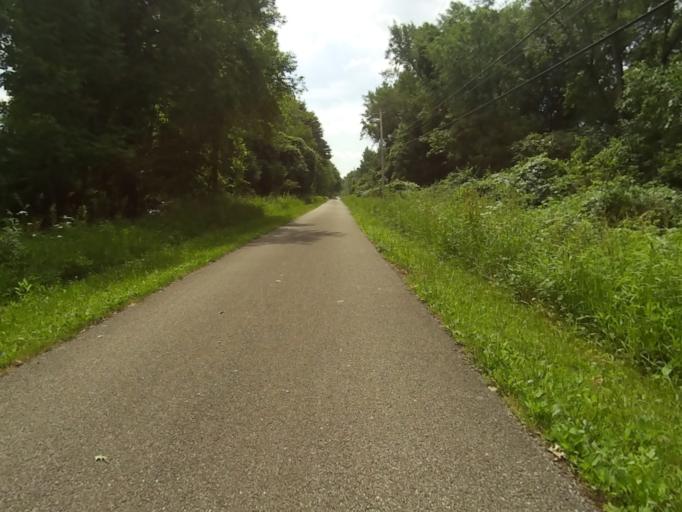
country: US
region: Ohio
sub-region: Summit County
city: Hudson
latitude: 41.2214
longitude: -81.4766
